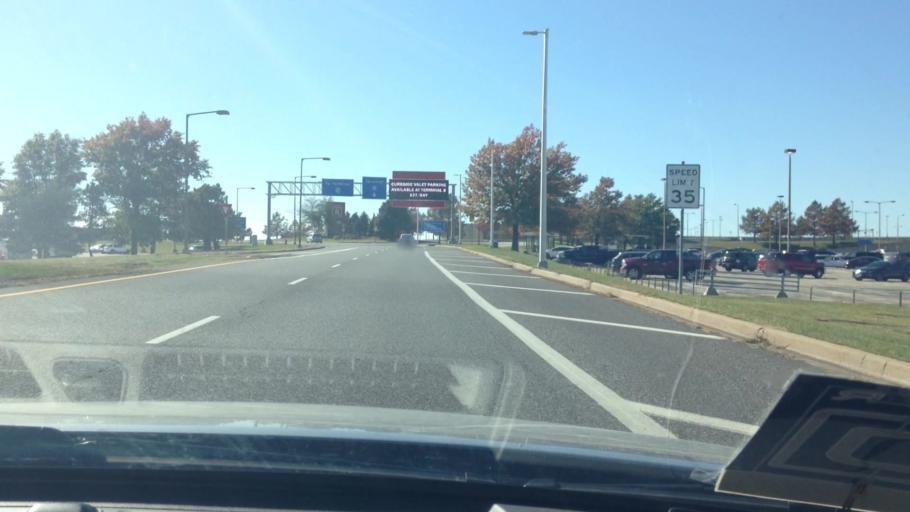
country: US
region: Missouri
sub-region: Platte County
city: Weatherby Lake
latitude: 39.2997
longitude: -94.7163
